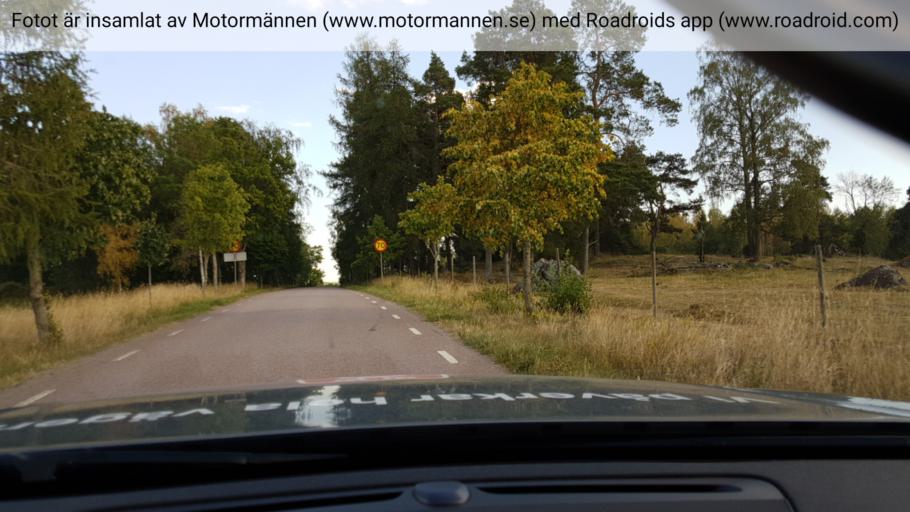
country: SE
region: Vaestmanland
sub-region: Vasteras
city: Tillberga
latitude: 59.6867
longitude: 16.6885
